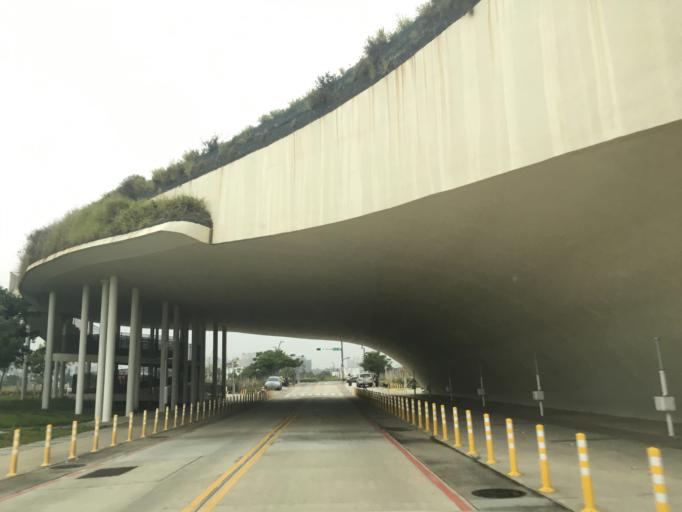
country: TW
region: Taiwan
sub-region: Taichung City
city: Taichung
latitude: 24.1909
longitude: 120.6552
